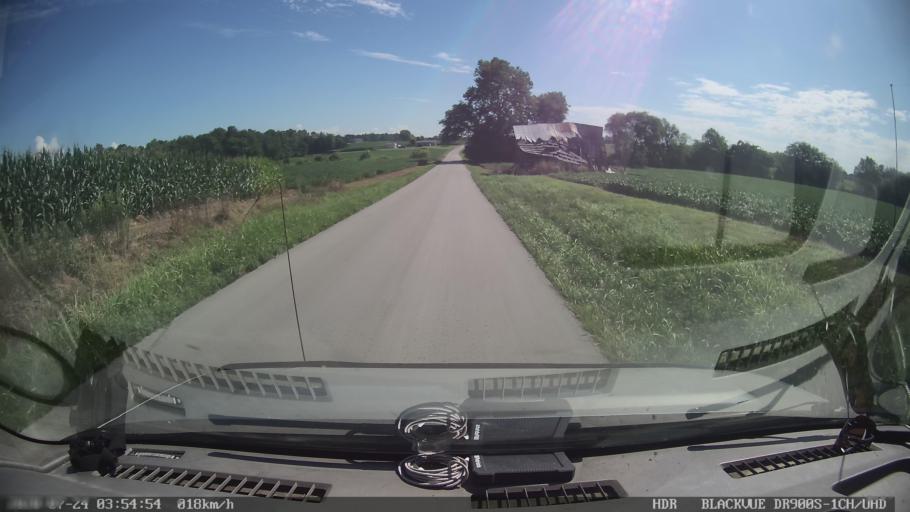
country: US
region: Kentucky
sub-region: Todd County
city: Elkton
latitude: 36.7801
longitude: -87.2325
